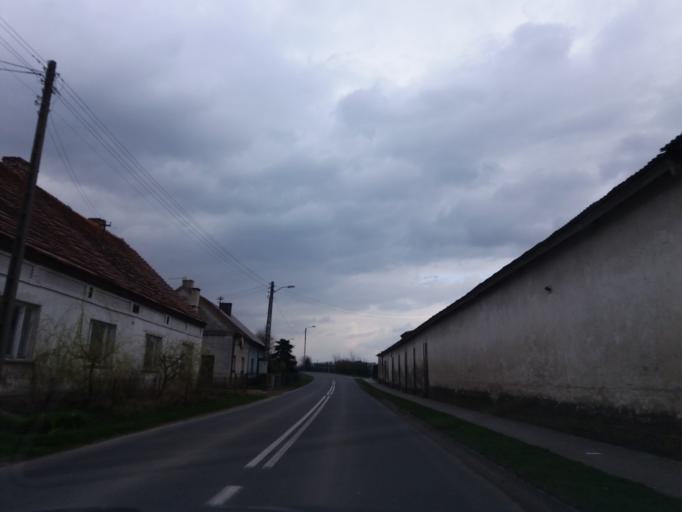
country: PL
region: West Pomeranian Voivodeship
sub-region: Powiat pyrzycki
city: Przelewice
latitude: 53.1694
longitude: 15.0481
